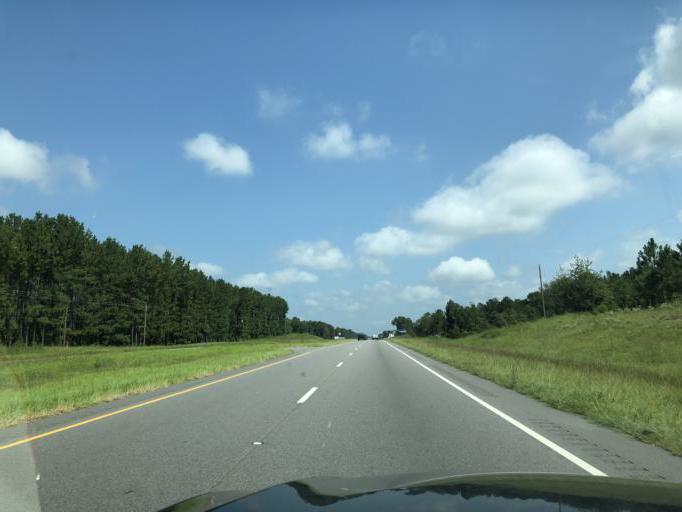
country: US
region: Alabama
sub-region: Houston County
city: Cottonwood
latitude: 31.0119
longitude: -85.4077
